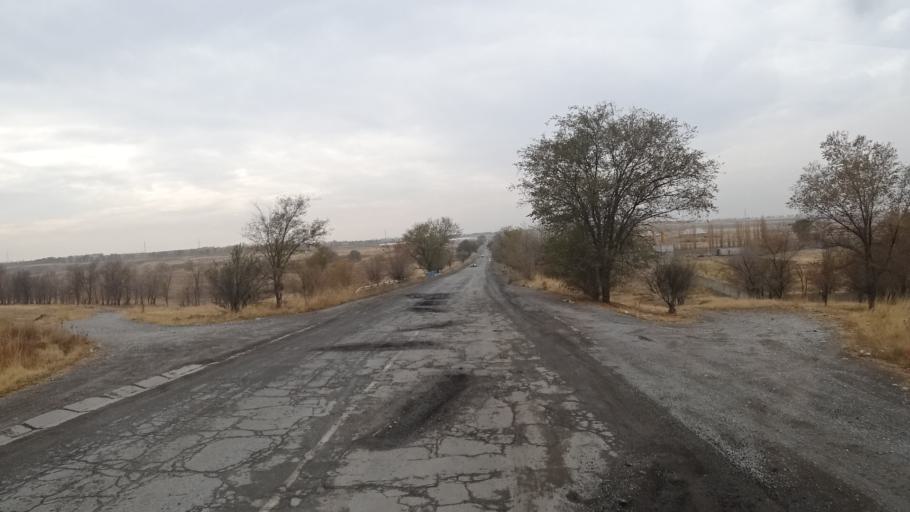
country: KZ
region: Ongtustik Qazaqstan
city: Aksu
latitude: 42.4278
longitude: 69.7067
